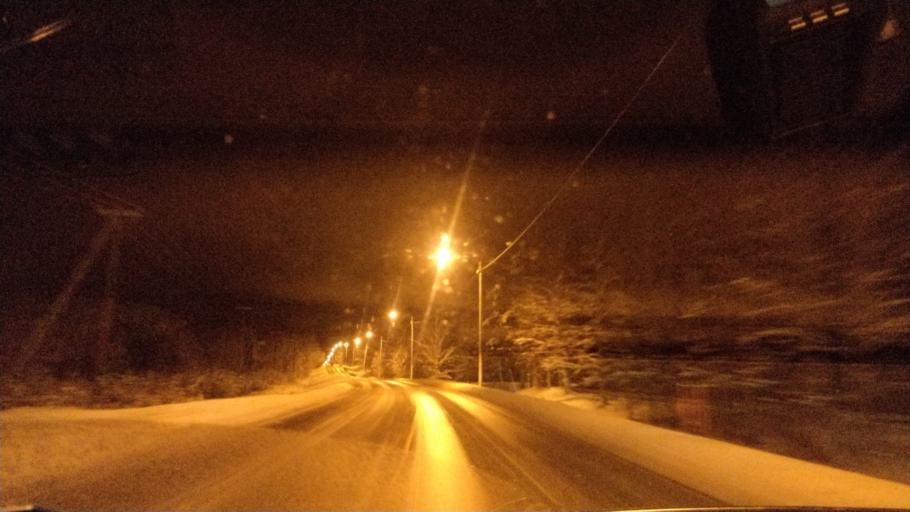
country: FI
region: Lapland
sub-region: Rovaniemi
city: Rovaniemi
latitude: 66.3020
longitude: 25.3544
